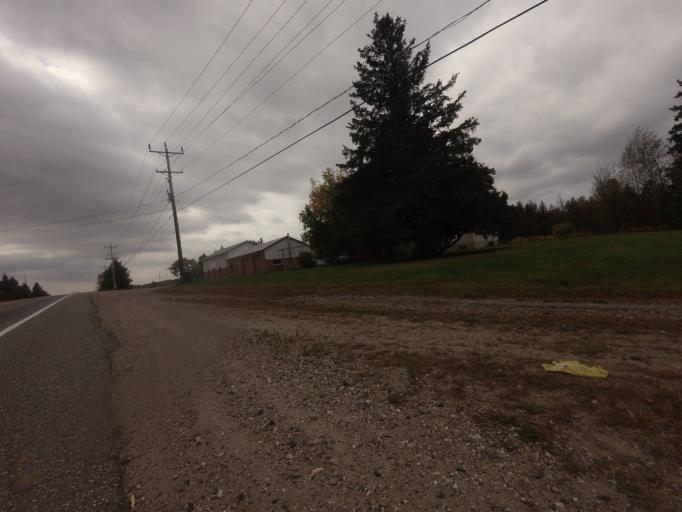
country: CA
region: Quebec
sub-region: Outaouais
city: Wakefield
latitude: 45.9199
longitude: -76.0173
